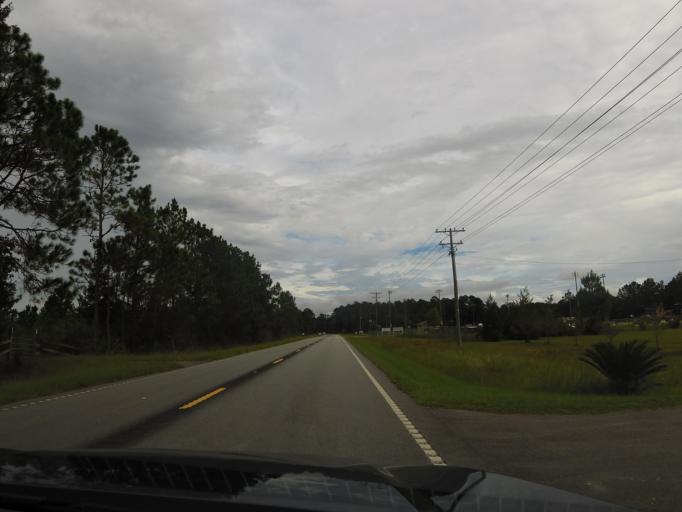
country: US
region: Florida
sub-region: Nassau County
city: Hilliard
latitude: 30.5213
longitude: -82.0551
